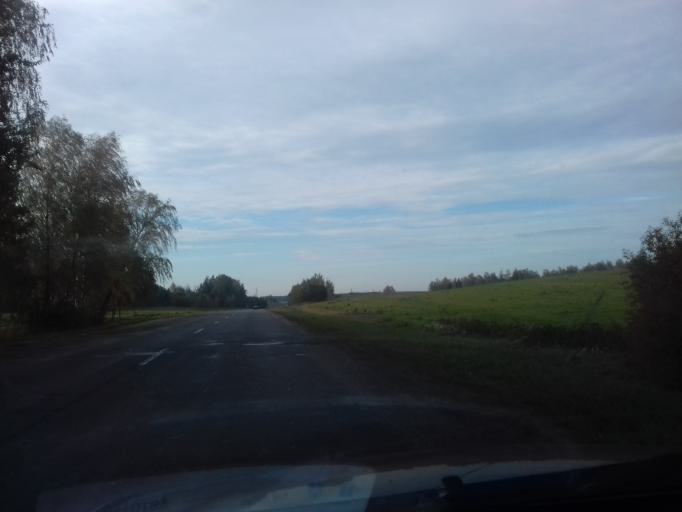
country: BY
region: Minsk
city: Hatava
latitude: 53.7635
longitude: 27.6443
